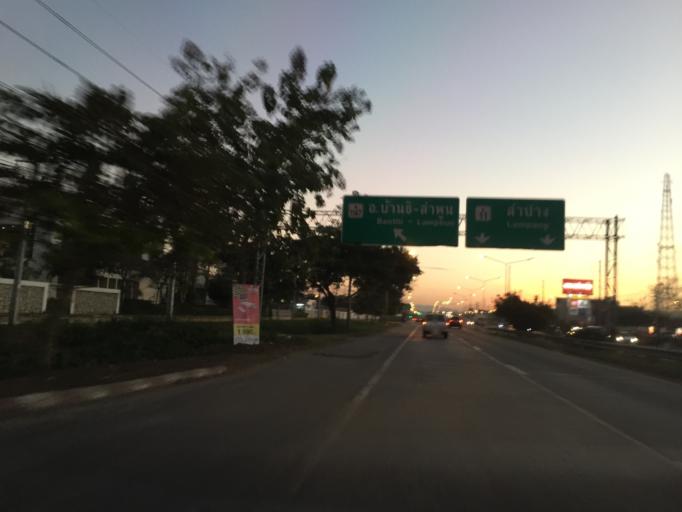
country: TH
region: Lamphun
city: Lamphun
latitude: 18.5949
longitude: 99.0428
